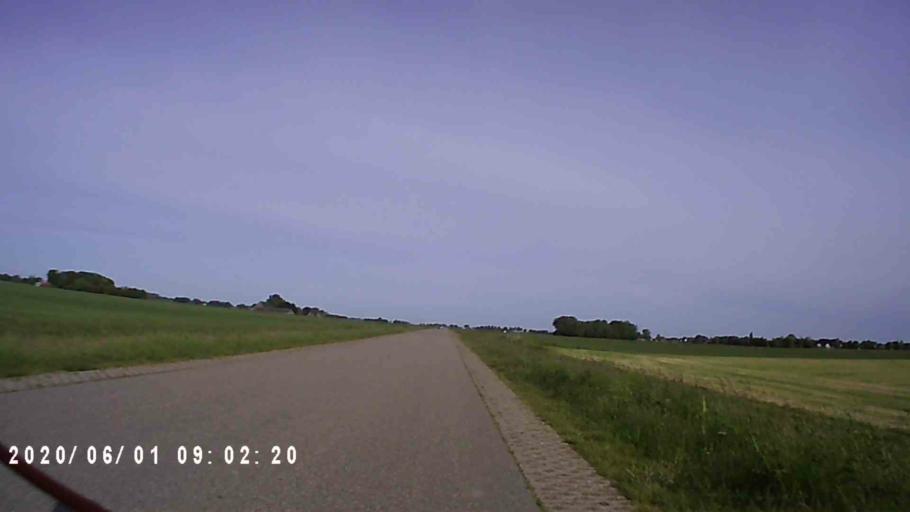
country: NL
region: Friesland
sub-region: Gemeente Ferwerderadiel
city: Hallum
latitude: 53.2925
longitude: 5.7865
